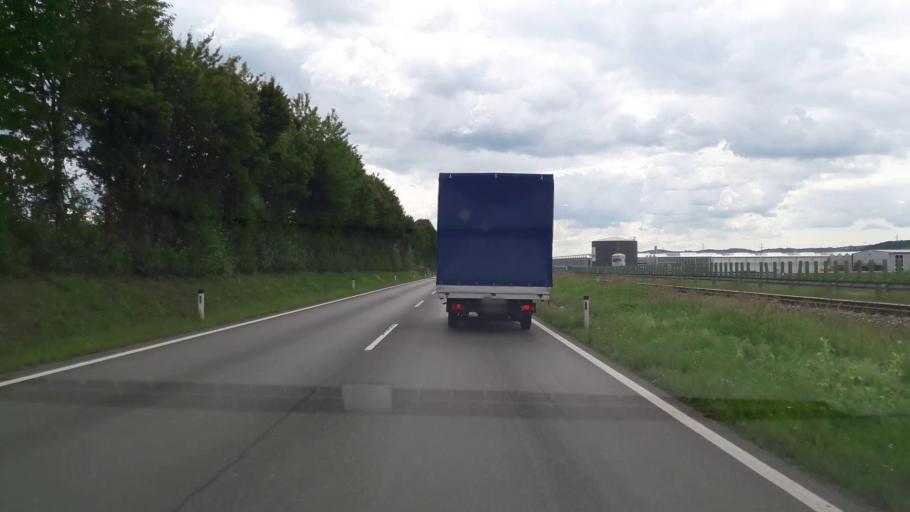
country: AT
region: Styria
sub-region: Politischer Bezirk Weiz
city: Sankt Ruprecht an der Raab
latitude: 47.1322
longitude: 15.6851
